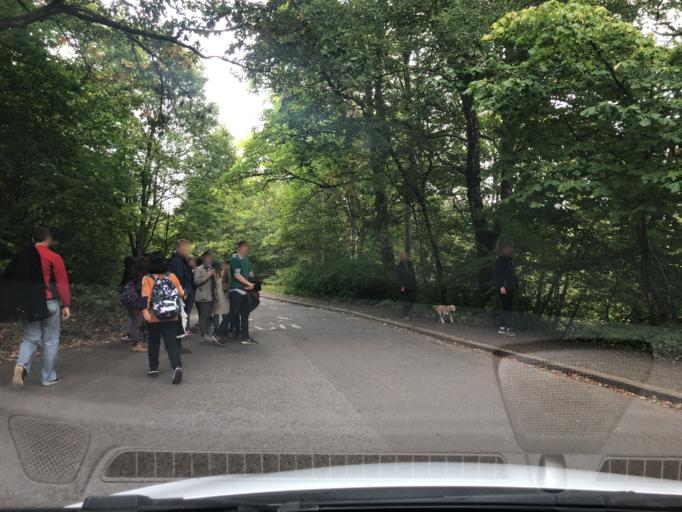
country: GB
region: Scotland
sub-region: Perth and Kinross
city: Bankfoot
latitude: 56.5611
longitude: -3.6078
